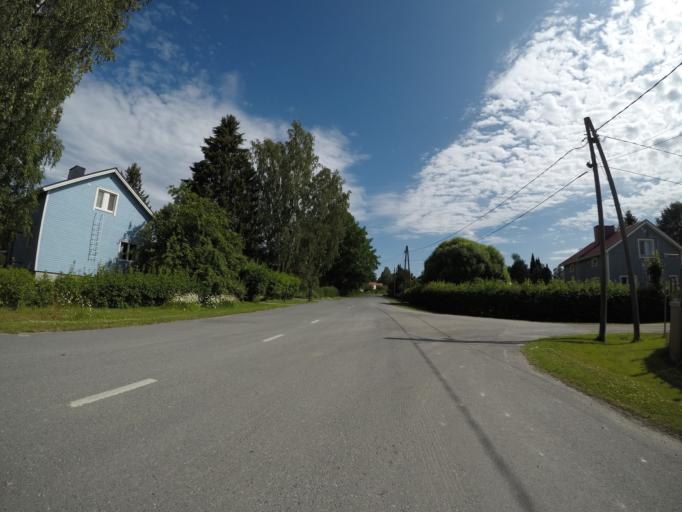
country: FI
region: Haeme
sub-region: Haemeenlinna
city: Haemeenlinna
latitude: 60.9893
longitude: 24.4045
